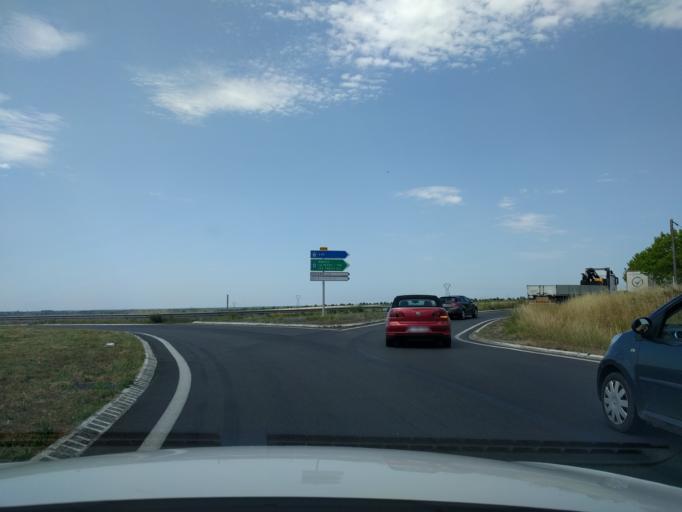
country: FR
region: Poitou-Charentes
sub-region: Departement des Deux-Sevres
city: Bessines
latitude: 46.3493
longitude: -0.5127
